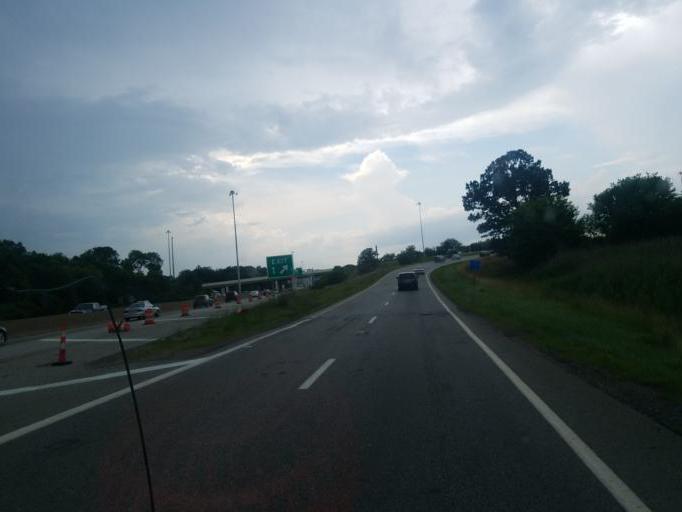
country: US
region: Ohio
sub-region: Summit County
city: Portage Lakes
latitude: 41.0357
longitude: -81.5628
